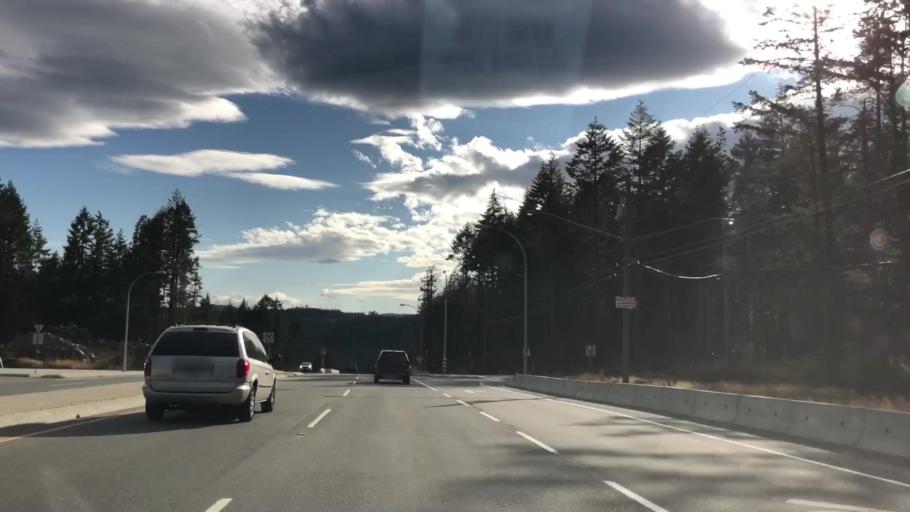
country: CA
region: British Columbia
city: Langford
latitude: 48.5667
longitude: -123.5612
